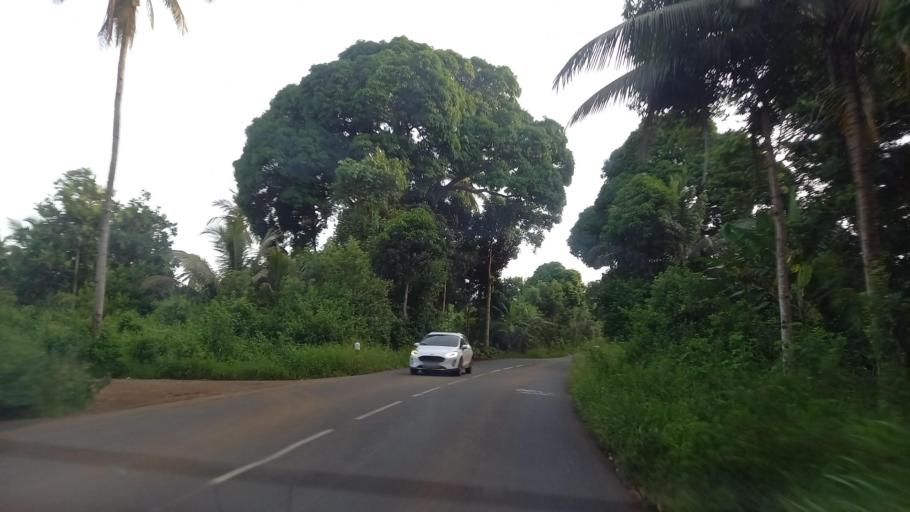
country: YT
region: M'Tsangamouji
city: M'Tsangamouji
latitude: -12.7497
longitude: 45.1151
